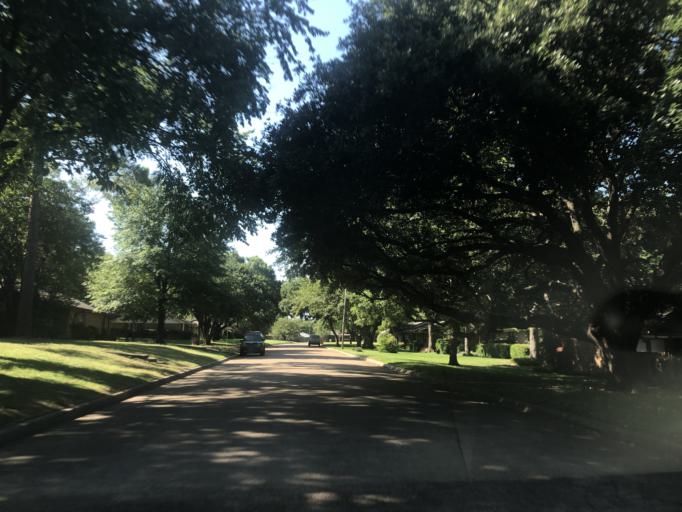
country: US
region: Texas
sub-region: Dallas County
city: Grand Prairie
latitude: 32.7672
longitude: -97.0189
